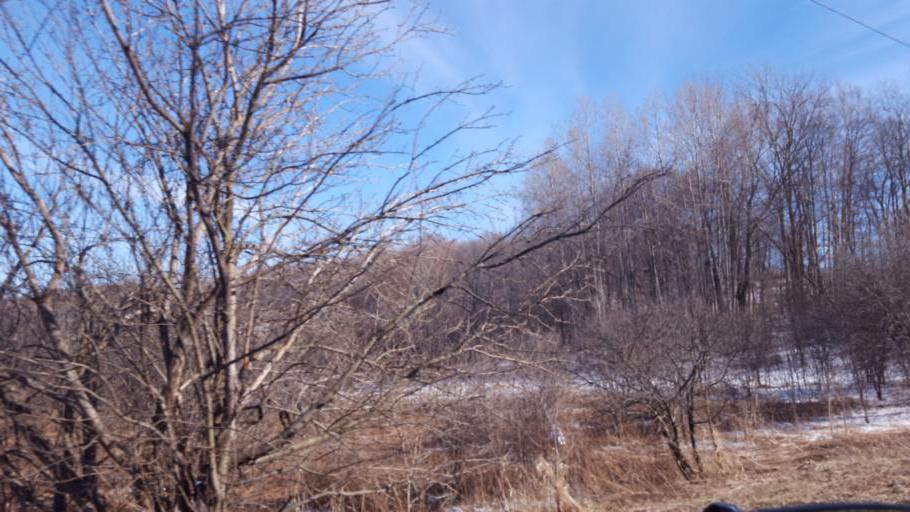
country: US
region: New York
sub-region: Allegany County
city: Wellsville
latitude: 42.1036
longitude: -77.9955
